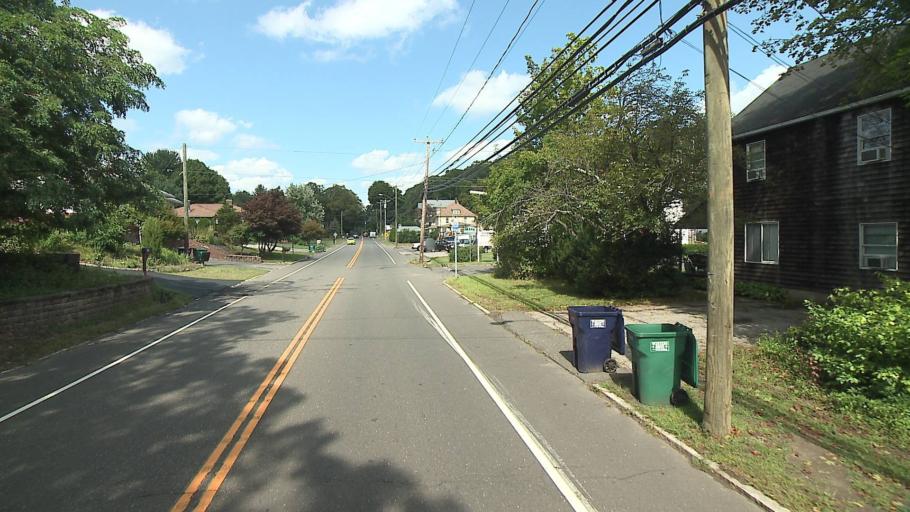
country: US
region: Connecticut
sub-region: New Haven County
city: Seymour
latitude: 41.3805
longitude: -73.0761
